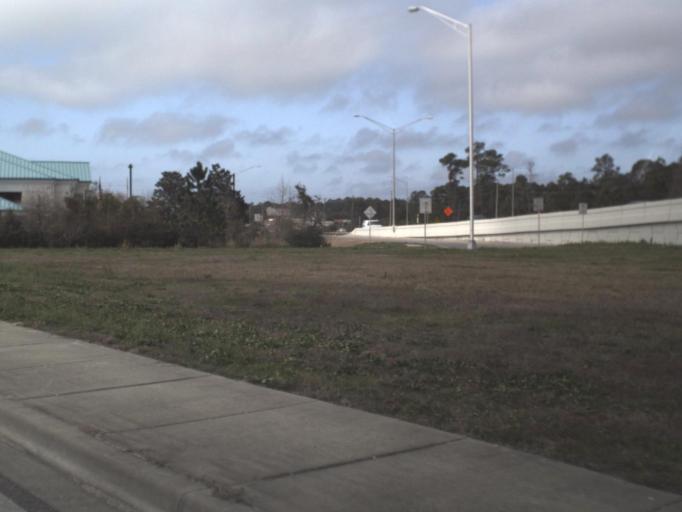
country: US
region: Florida
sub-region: Bay County
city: Upper Grand Lagoon
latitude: 30.1879
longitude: -85.7657
